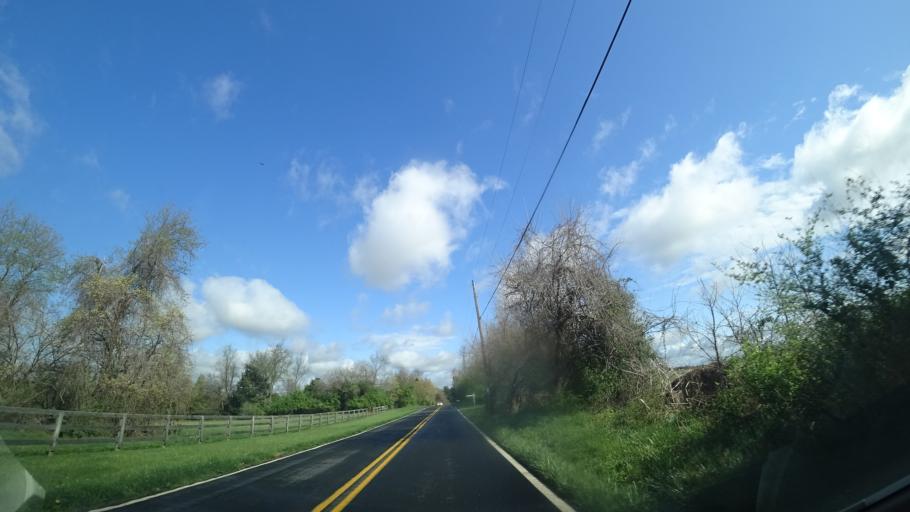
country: US
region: Maryland
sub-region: Montgomery County
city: Poolesville
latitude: 39.1097
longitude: -77.3798
